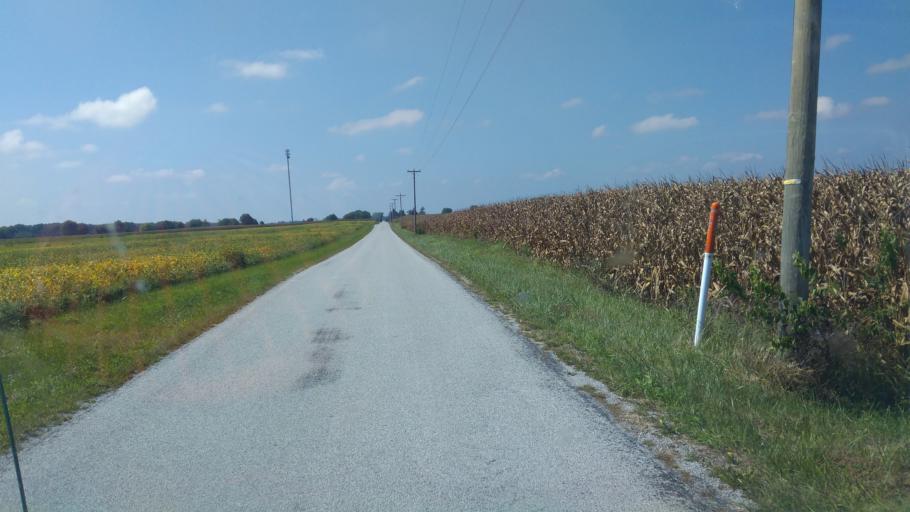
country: US
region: Ohio
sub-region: Hardin County
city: Kenton
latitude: 40.6742
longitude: -83.5990
